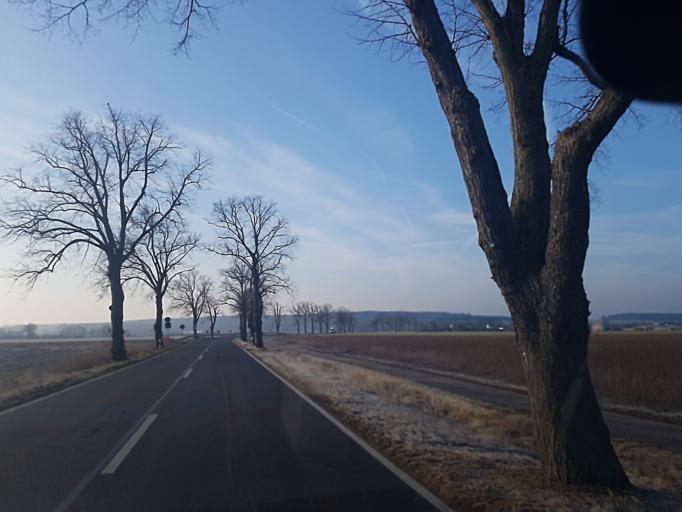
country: DE
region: Brandenburg
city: Golzow
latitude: 52.2485
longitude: 12.5918
